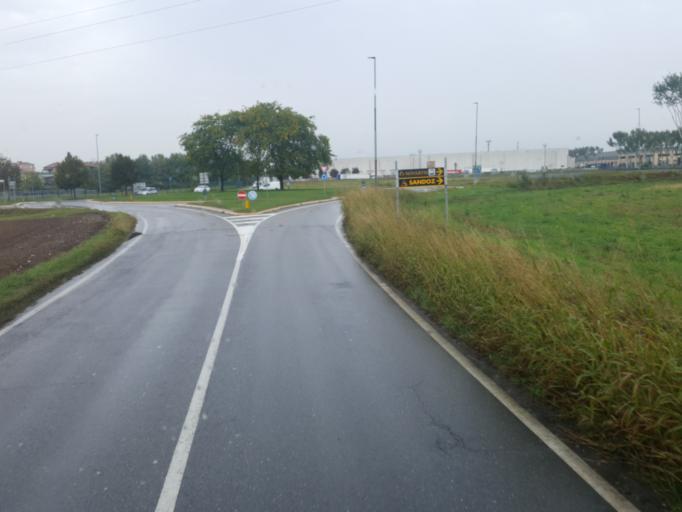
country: IT
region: Lombardy
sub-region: Provincia di Varese
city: Origgio
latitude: 45.5884
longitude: 9.0241
